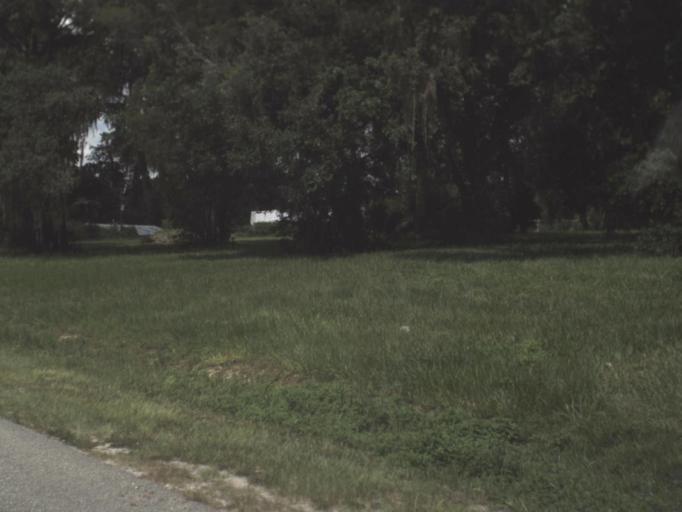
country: US
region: Florida
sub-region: Hernando County
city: Brooksville
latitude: 28.5912
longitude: -82.3721
